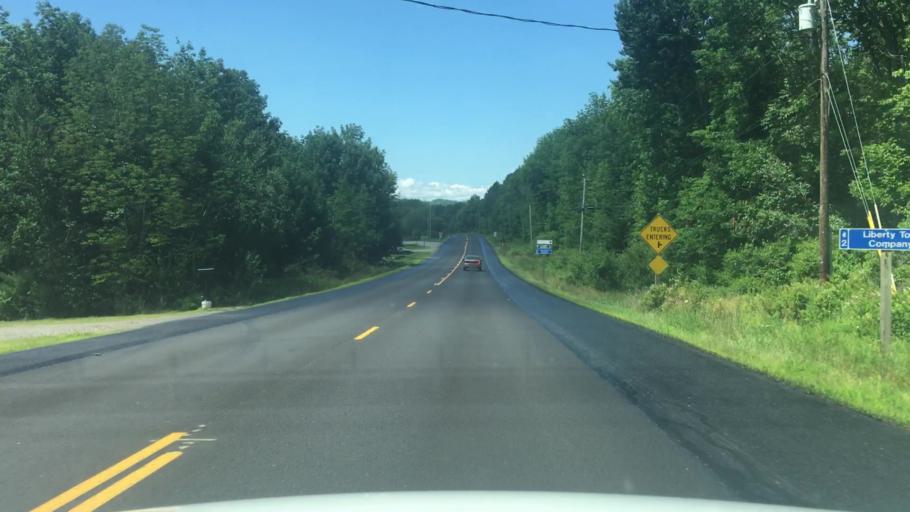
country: US
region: Maine
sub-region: Waldo County
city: Searsmont
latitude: 44.4020
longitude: -69.2665
